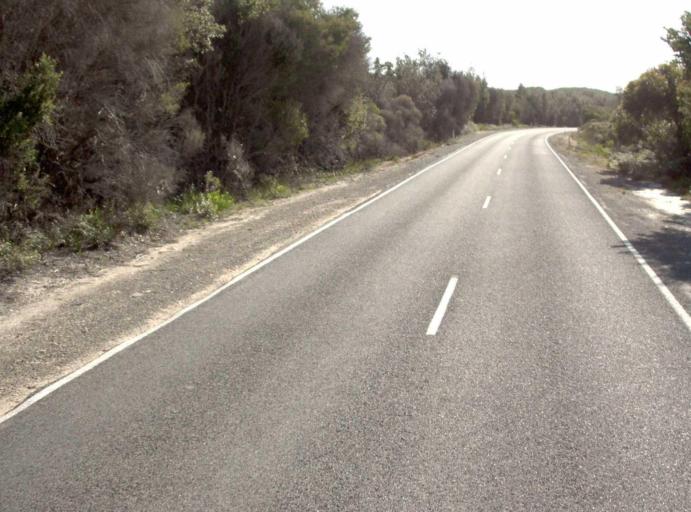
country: AU
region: Victoria
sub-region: East Gippsland
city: Lakes Entrance
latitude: -37.8015
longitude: 148.7292
